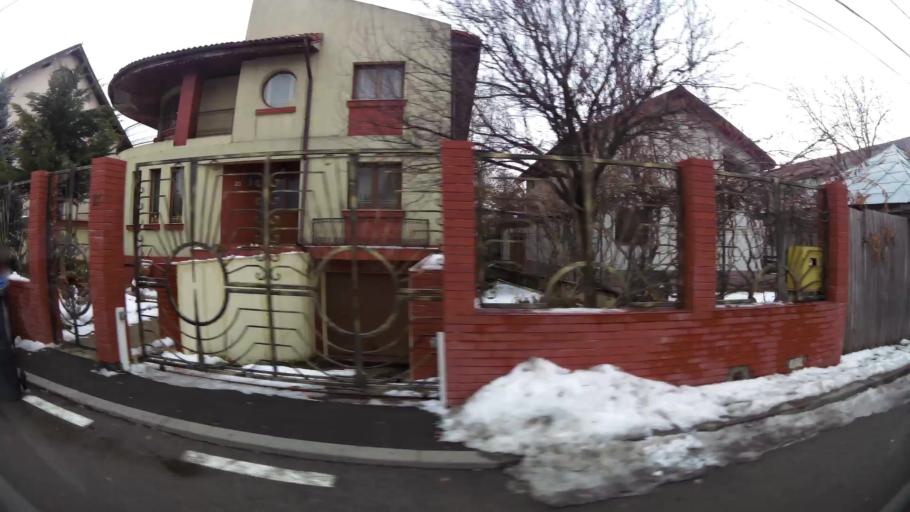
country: RO
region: Ilfov
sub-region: Comuna Otopeni
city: Otopeni
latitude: 44.5450
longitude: 26.0719
